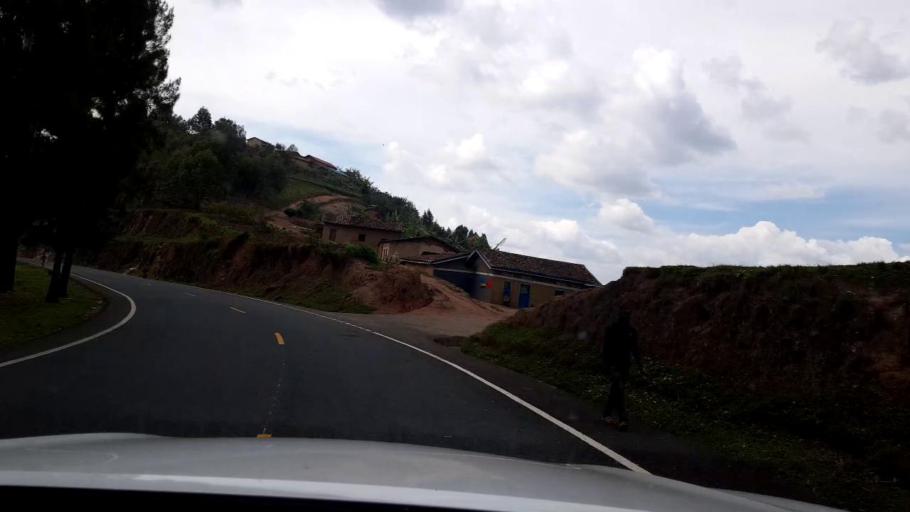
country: RW
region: Southern Province
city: Gitarama
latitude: -2.0257
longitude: 29.7175
